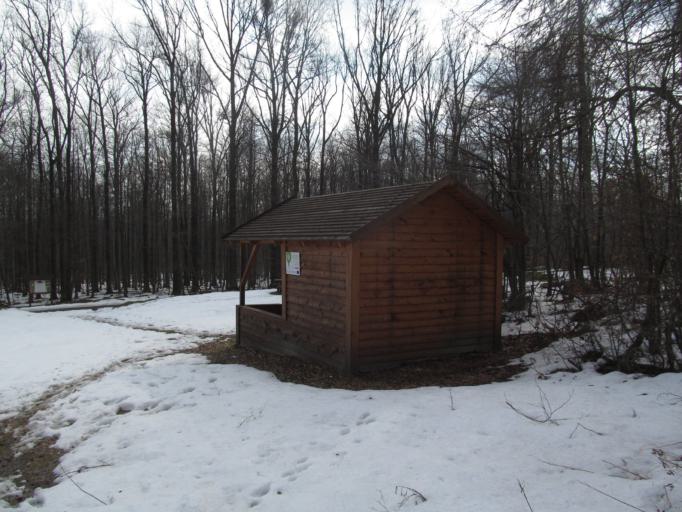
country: HU
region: Gyor-Moson-Sopron
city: Bakonyszentlaszlo
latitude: 47.2925
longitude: 17.7720
